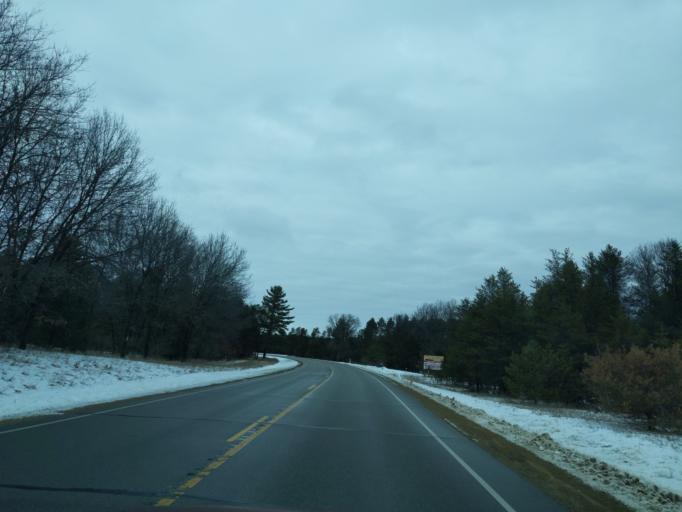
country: US
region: Wisconsin
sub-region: Waushara County
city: Wautoma
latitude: 43.9547
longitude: -89.3174
